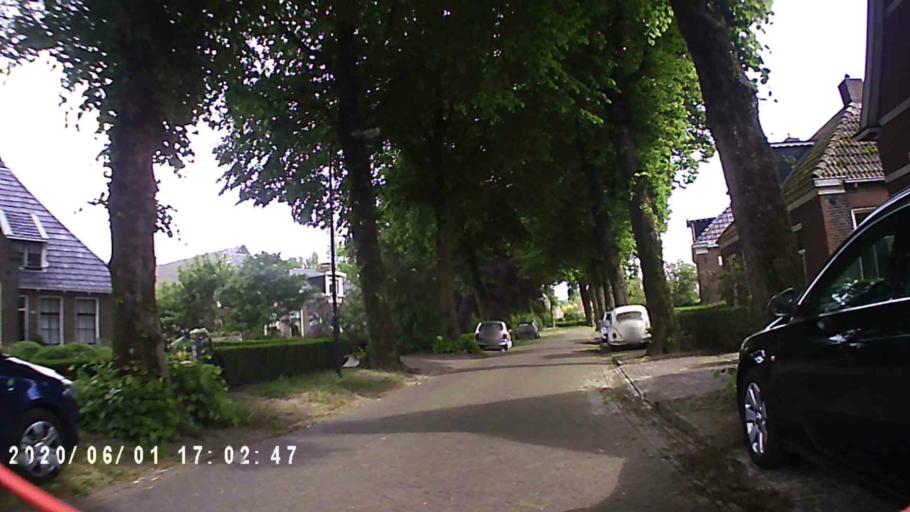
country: NL
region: Friesland
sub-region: Gemeente Tytsjerksteradiel
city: Hurdegaryp
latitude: 53.1780
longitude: 5.9287
